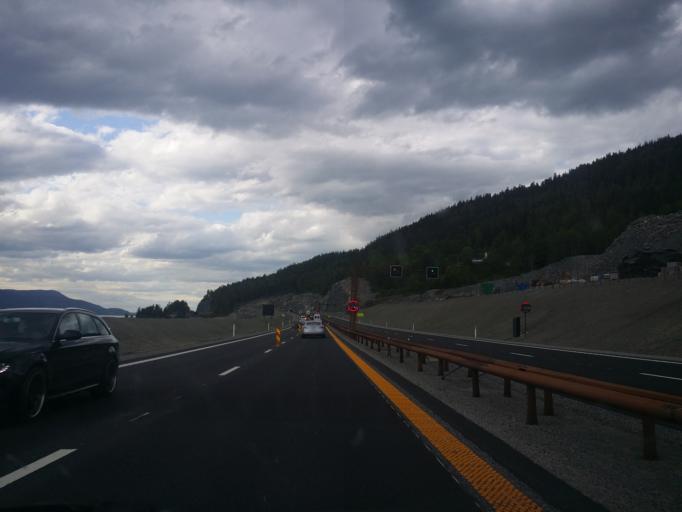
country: NO
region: Akershus
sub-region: Eidsvoll
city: Eidsvoll
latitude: 60.4242
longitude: 11.2406
